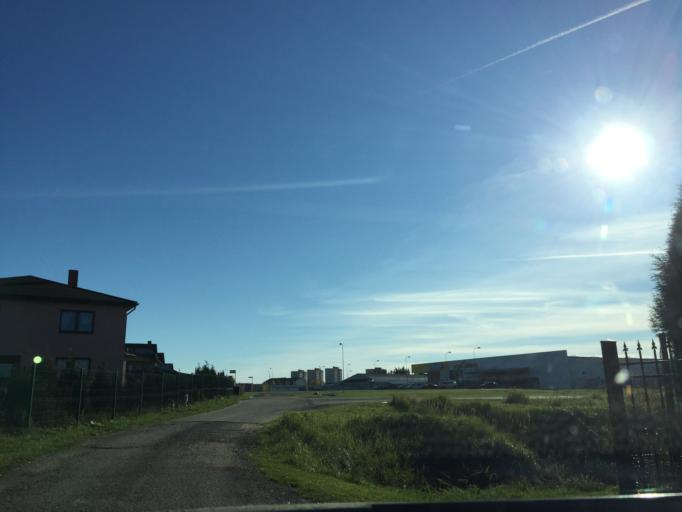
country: LV
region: Aizkraukles Rajons
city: Aizkraukle
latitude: 56.6121
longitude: 25.2603
